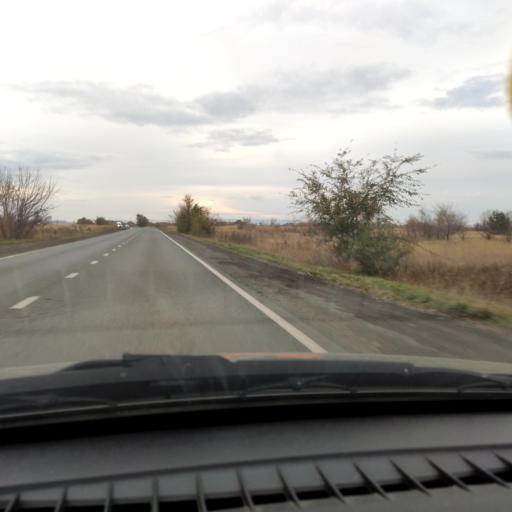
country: RU
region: Samara
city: Podstepki
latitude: 53.5206
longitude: 49.2034
